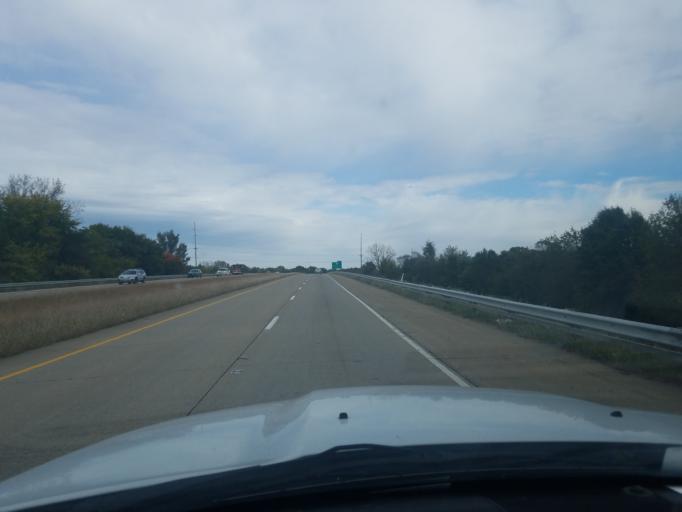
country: US
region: Indiana
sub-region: Warrick County
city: Newburgh
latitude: 37.9460
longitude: -87.4741
